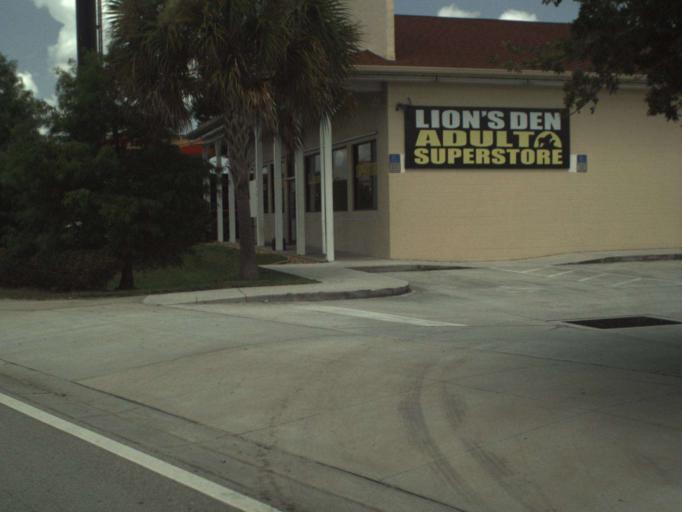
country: US
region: Florida
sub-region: Saint Lucie County
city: Fort Pierce South
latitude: 27.4133
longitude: -80.3970
